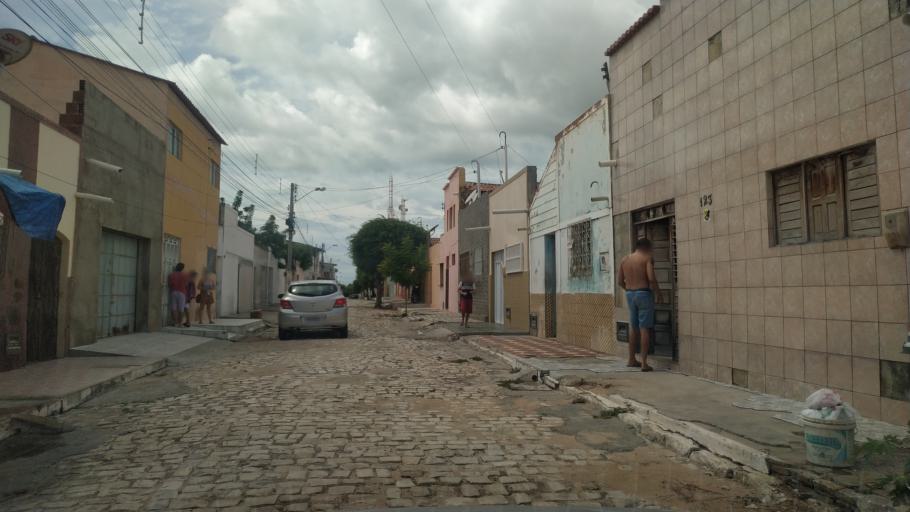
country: BR
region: Rio Grande do Norte
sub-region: Areia Branca
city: Areia Branca
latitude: -4.9561
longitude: -37.1346
